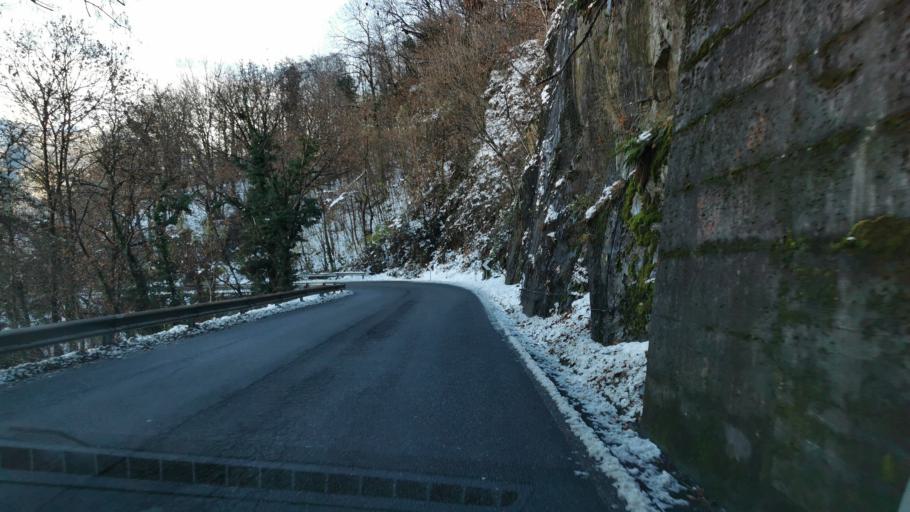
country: IT
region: Lombardy
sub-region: Provincia di Sondrio
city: Cosio Valtellino
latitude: 46.1276
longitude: 9.5528
